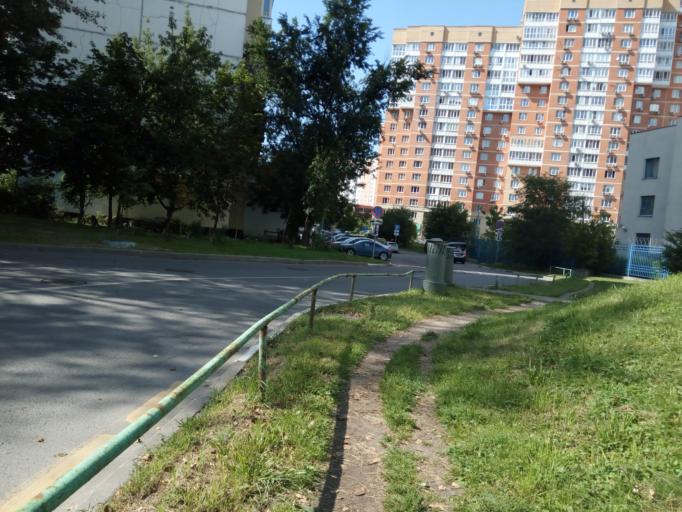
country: RU
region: Moscow
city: Sokol
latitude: 55.7786
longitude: 37.5358
